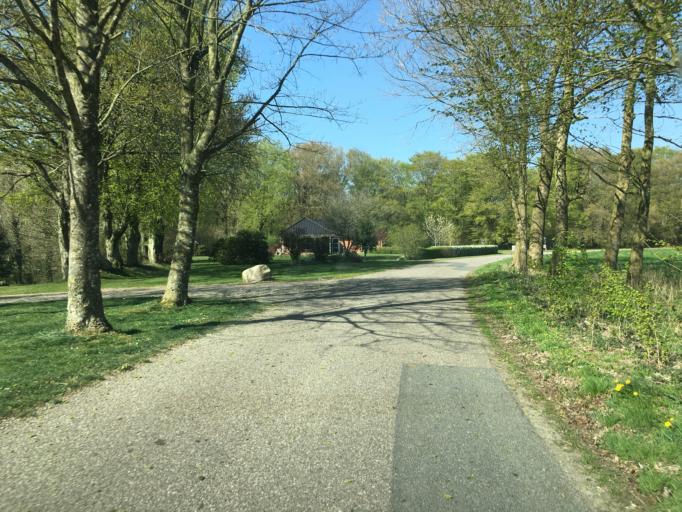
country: DK
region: South Denmark
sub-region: Aabenraa Kommune
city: Rodekro
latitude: 55.1040
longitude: 9.2377
